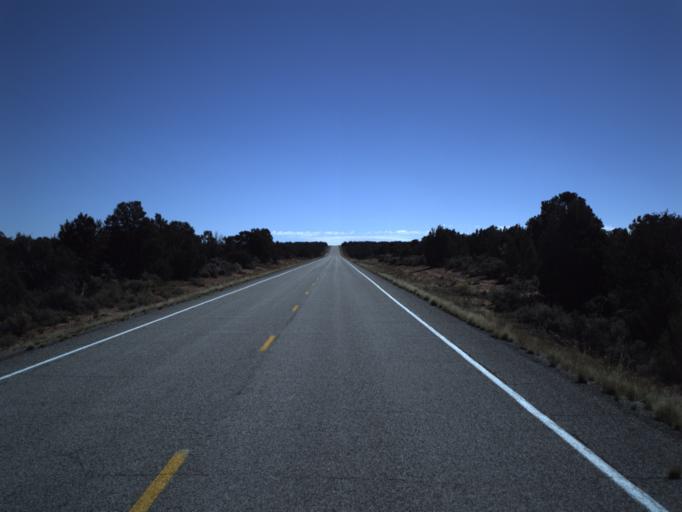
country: US
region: Utah
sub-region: San Juan County
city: Blanding
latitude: 37.5553
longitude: -109.9984
